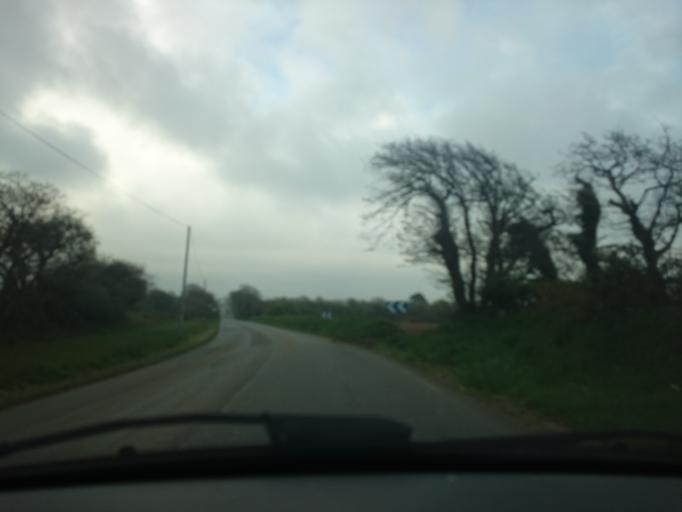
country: FR
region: Brittany
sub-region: Departement du Finistere
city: Lanrivoare
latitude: 48.4819
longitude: -4.6635
